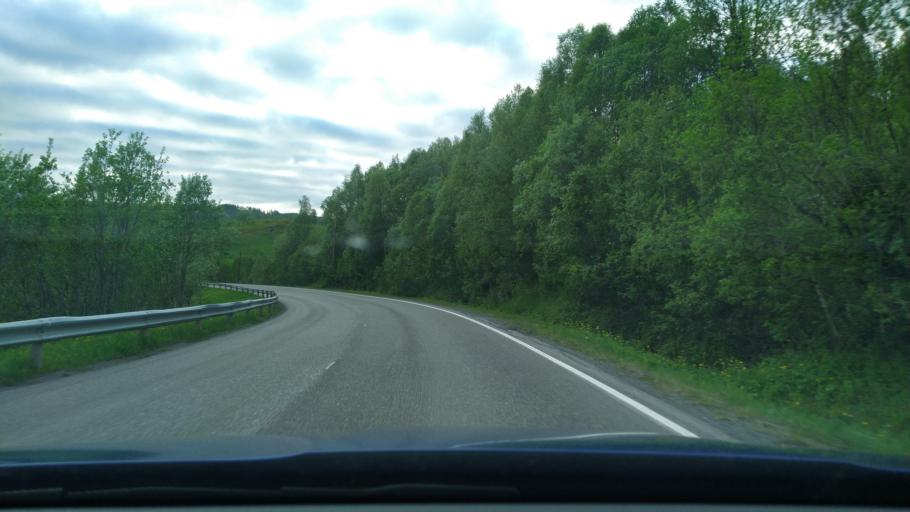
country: NO
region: Troms
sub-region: Sorreisa
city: Sorreisa
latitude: 69.0944
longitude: 18.3387
